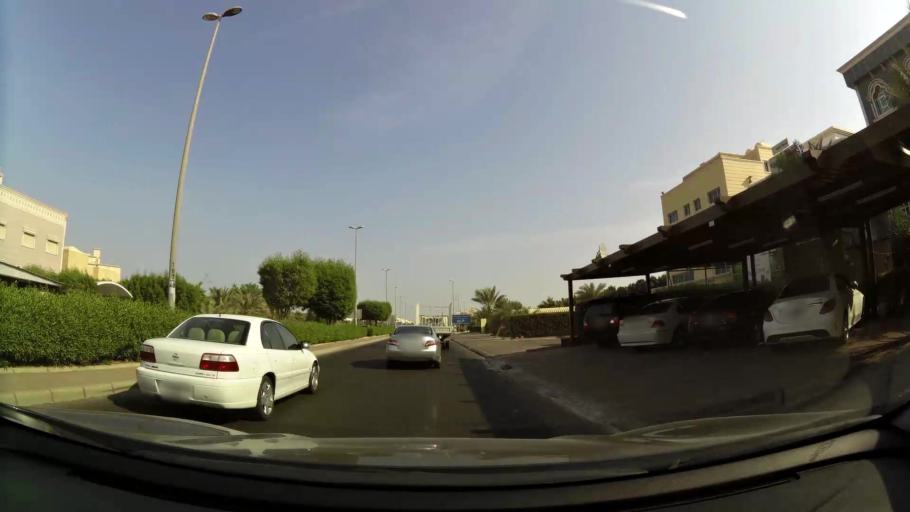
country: KW
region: Mubarak al Kabir
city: Mubarak al Kabir
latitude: 29.1973
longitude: 48.0894
